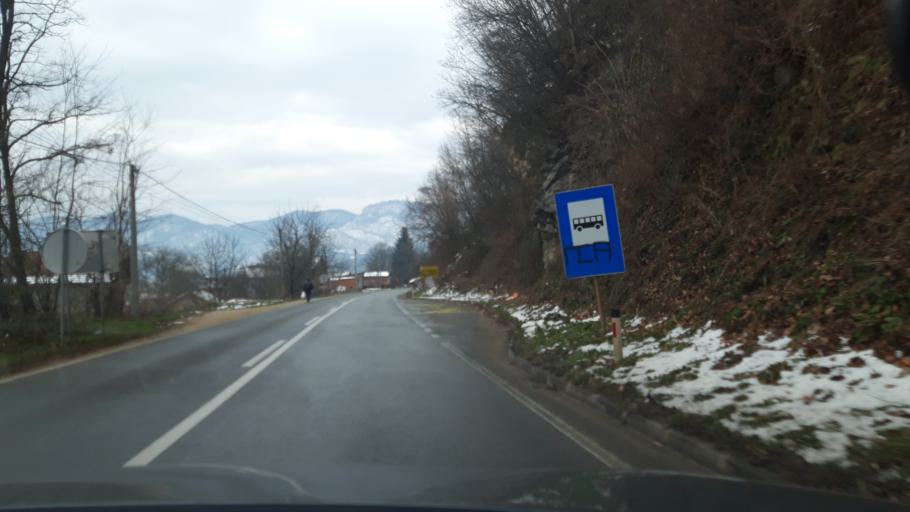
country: RS
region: Central Serbia
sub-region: Macvanski Okrug
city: Mali Zvornik
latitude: 44.2991
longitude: 19.1488
